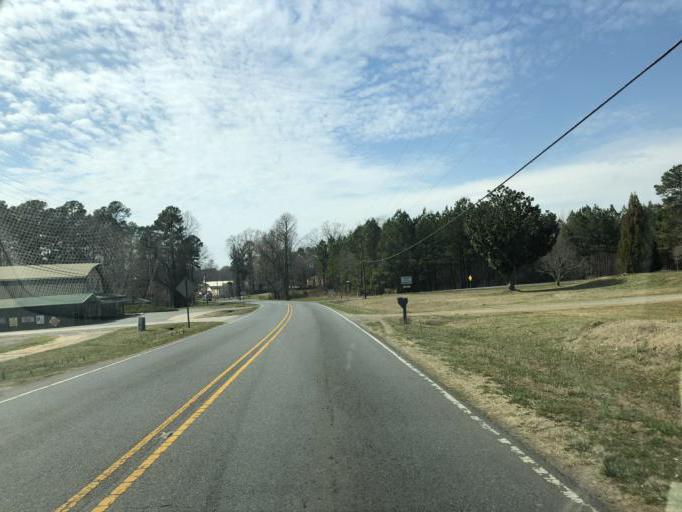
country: US
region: North Carolina
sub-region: Gaston County
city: Dallas
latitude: 35.3267
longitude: -81.1497
